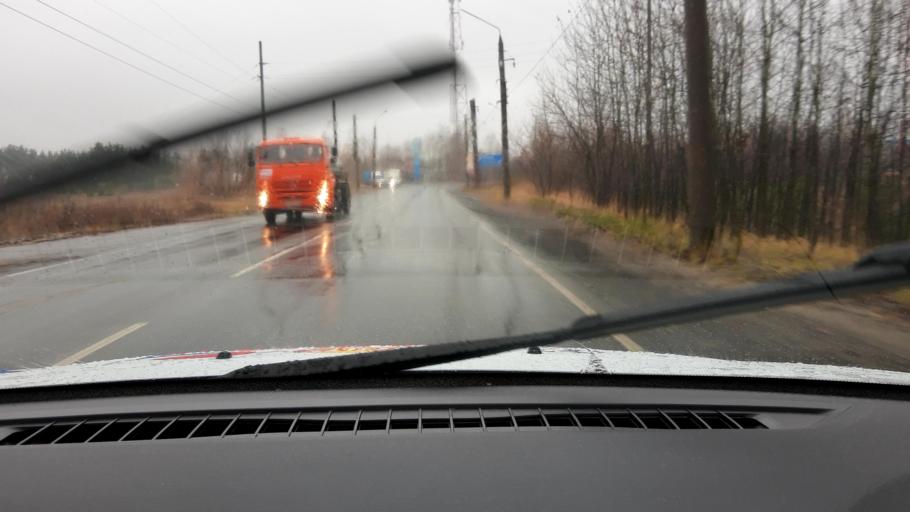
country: RU
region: Nizjnij Novgorod
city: Babino
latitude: 56.2905
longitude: 43.5952
